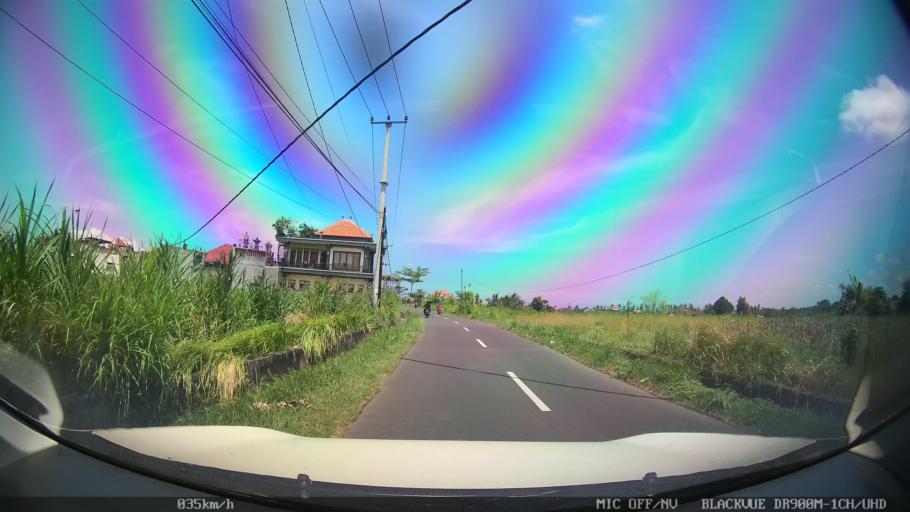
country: ID
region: Bali
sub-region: Kabupaten Gianyar
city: Ubud
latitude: -8.5628
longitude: 115.3194
